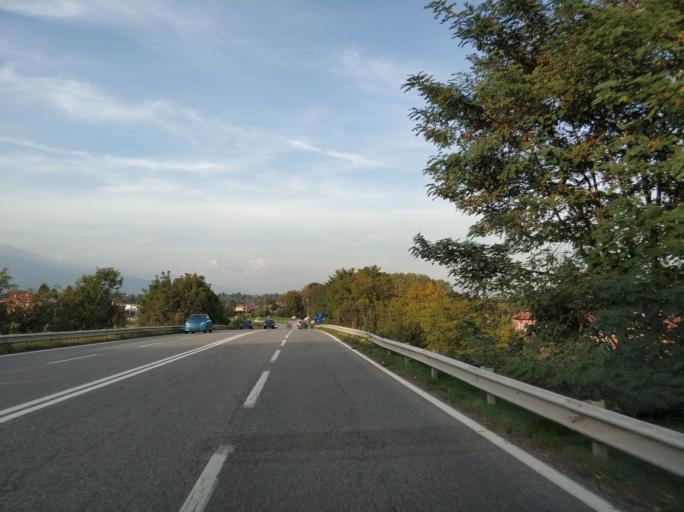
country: IT
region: Piedmont
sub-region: Provincia di Torino
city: Nole
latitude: 45.2385
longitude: 7.5815
